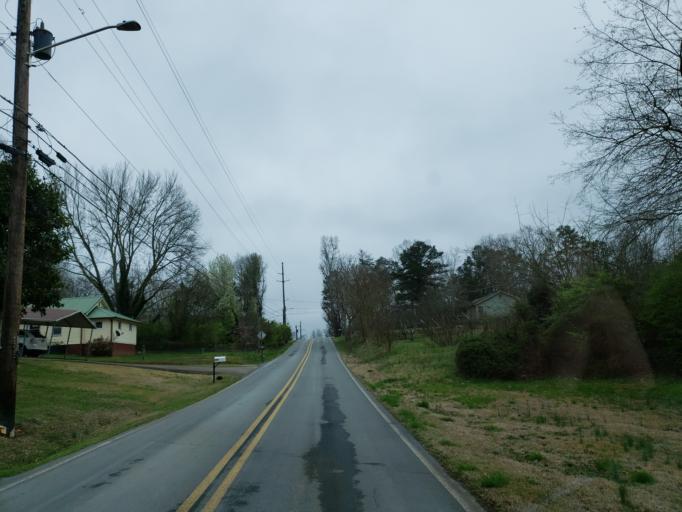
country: US
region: Georgia
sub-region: Pickens County
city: Jasper
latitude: 34.4631
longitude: -84.4220
